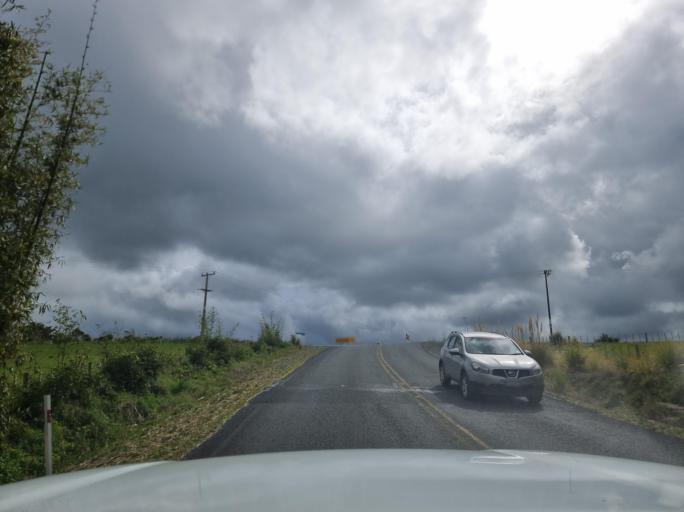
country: NZ
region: Northland
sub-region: Whangarei
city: Ruakaka
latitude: -36.1204
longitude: 174.1913
